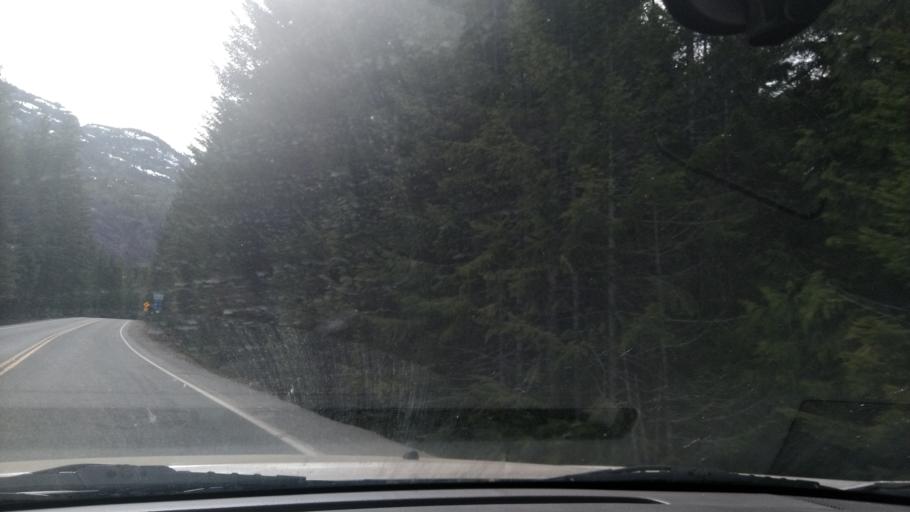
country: CA
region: British Columbia
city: Campbell River
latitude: 49.8411
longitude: -125.6402
